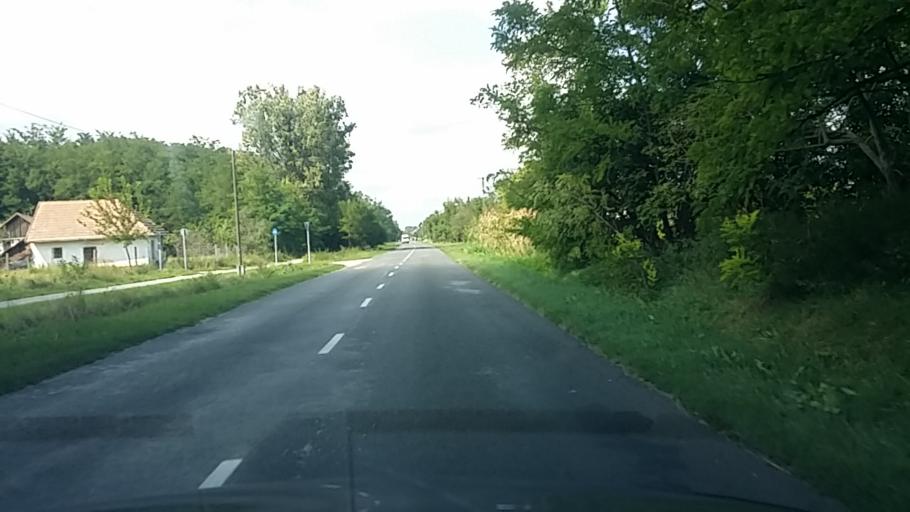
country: HU
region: Bacs-Kiskun
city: Tiszaalpar
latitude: 46.7470
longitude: 20.0441
